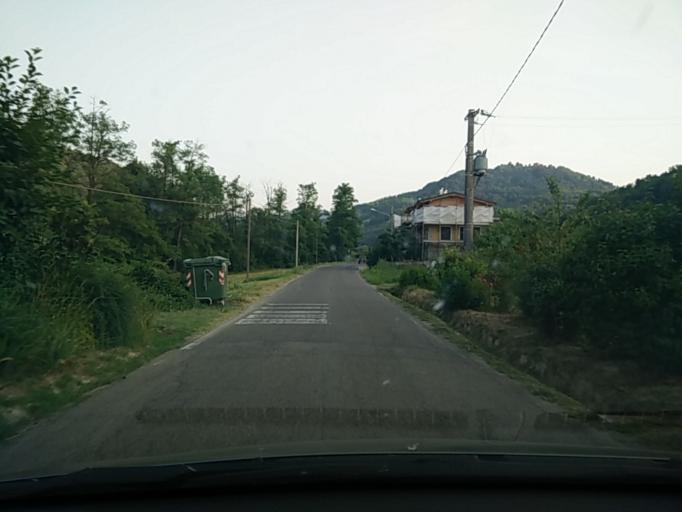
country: IT
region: Lombardy
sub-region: Provincia di Pavia
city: Torrazza Coste
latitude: 44.9632
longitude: 9.1029
